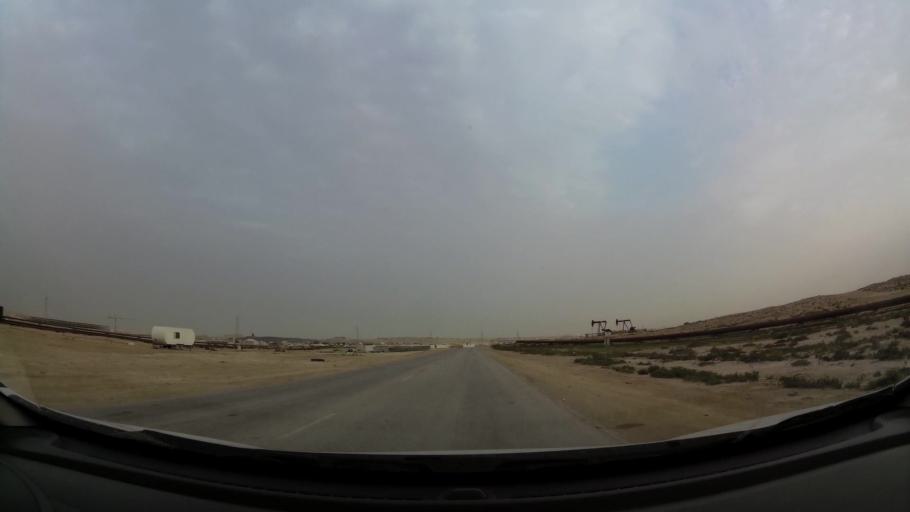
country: BH
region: Central Governorate
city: Dar Kulayb
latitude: 26.0148
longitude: 50.5777
